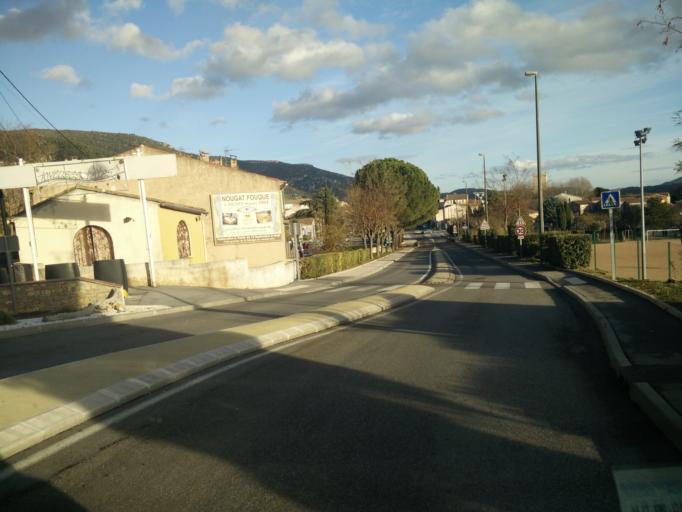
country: FR
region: Provence-Alpes-Cote d'Azur
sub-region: Departement du Var
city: Signes
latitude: 43.2903
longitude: 5.8598
